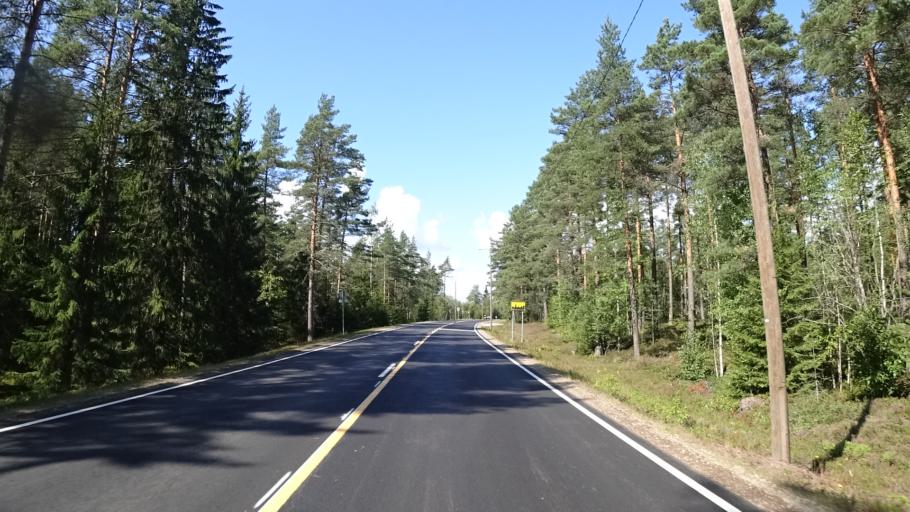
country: FI
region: Kymenlaakso
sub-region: Kotka-Hamina
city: Karhula
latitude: 60.5535
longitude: 26.9020
